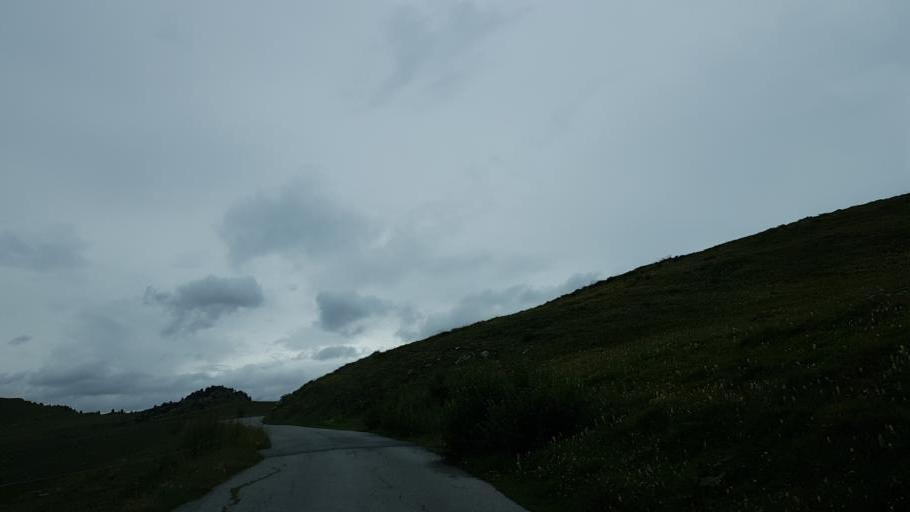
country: IT
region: Piedmont
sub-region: Provincia di Cuneo
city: Serre
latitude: 44.5441
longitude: 7.1184
